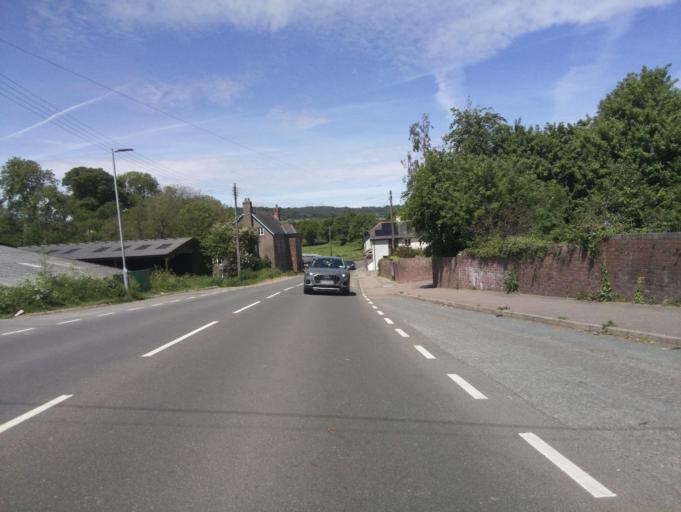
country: GB
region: England
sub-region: Devon
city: Honiton
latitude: 50.8086
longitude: -3.2310
